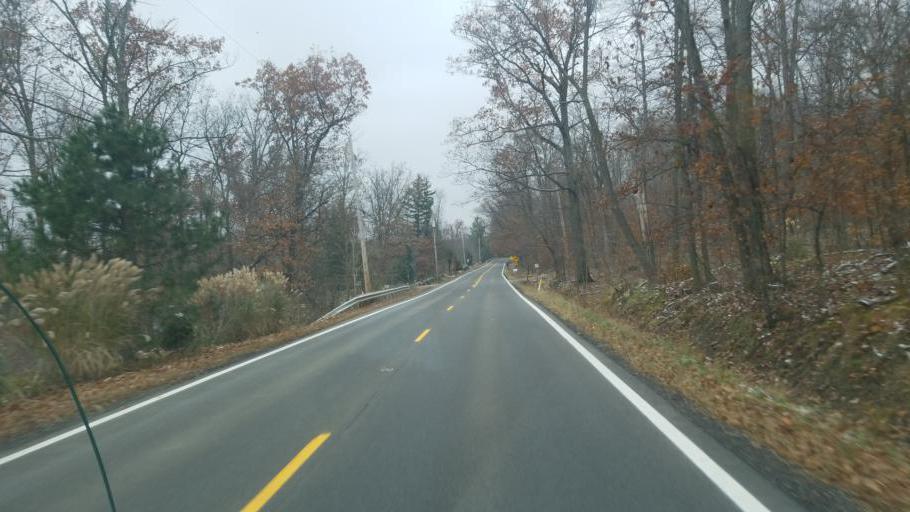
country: US
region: Ohio
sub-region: Cuyahoga County
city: North Royalton
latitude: 41.2708
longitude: -81.7251
